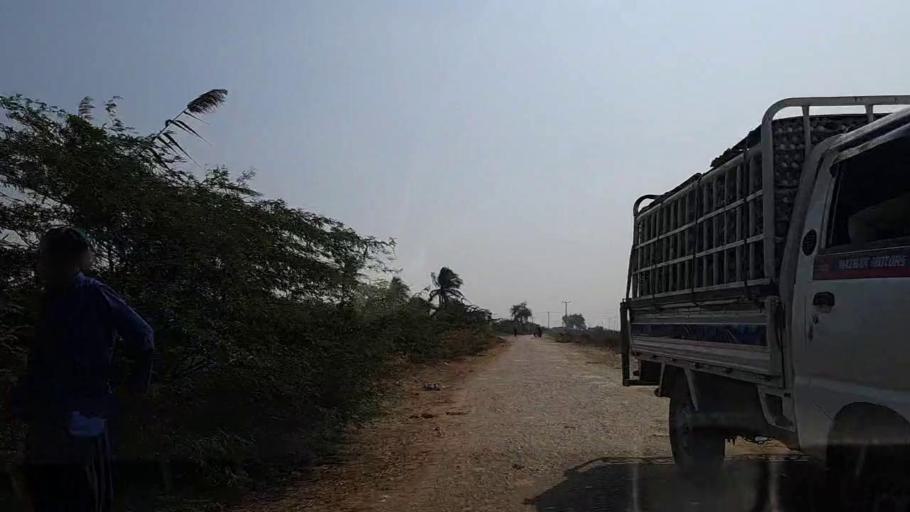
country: PK
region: Sindh
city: Thatta
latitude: 24.7411
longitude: 67.7688
